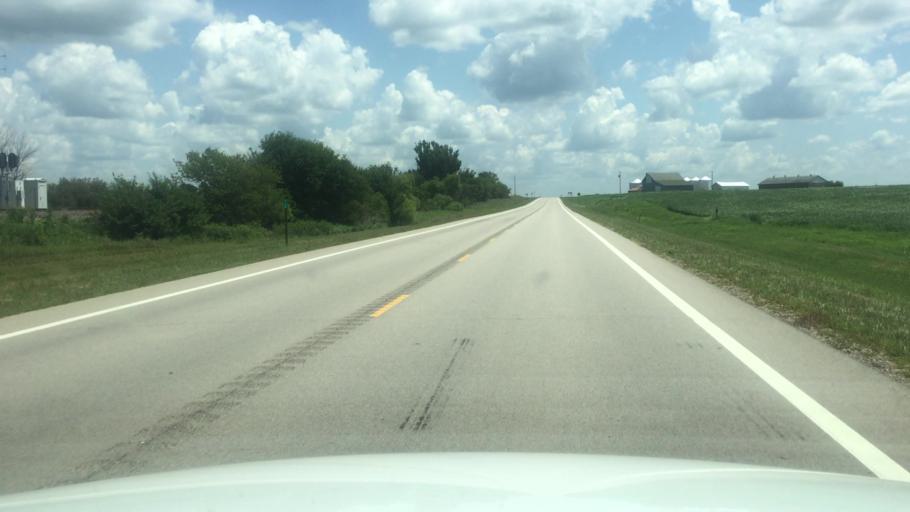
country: US
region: Kansas
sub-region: Brown County
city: Horton
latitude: 39.6544
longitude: -95.3676
